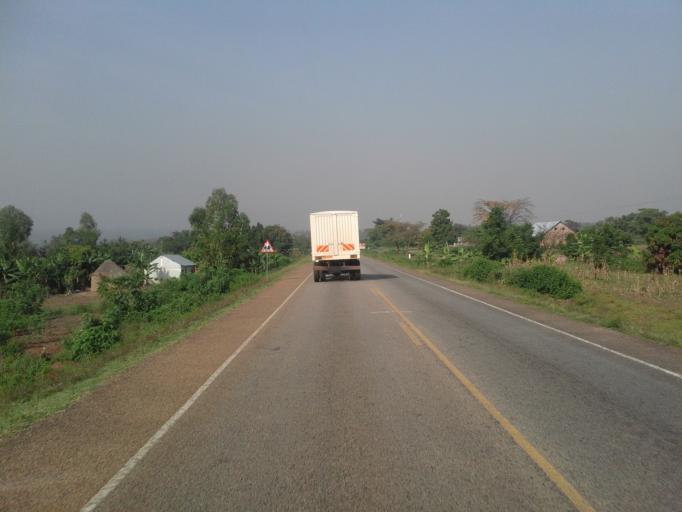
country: UG
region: Eastern Region
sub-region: Budaka District
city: Budaka
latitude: 1.0389
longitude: 34.0150
